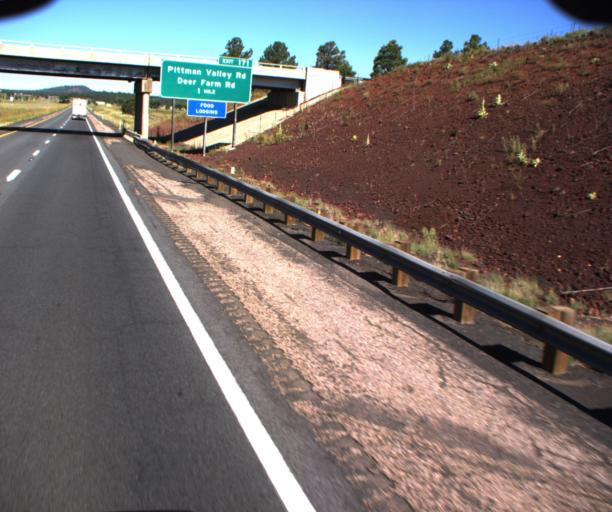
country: US
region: Arizona
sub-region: Coconino County
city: Parks
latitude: 35.2602
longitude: -112.0300
